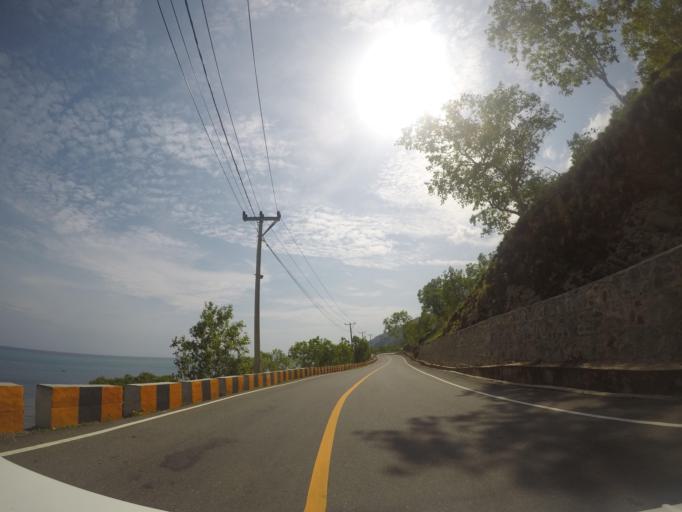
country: TL
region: Manatuto
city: Manatuto
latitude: -8.4789
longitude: 125.9113
